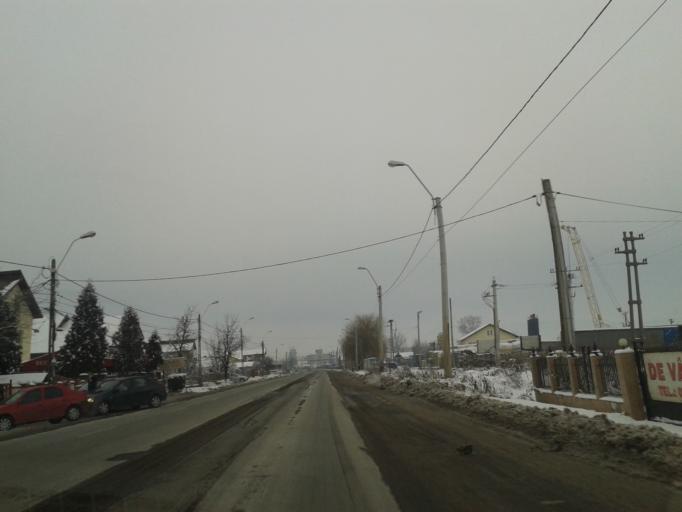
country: RO
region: Hunedoara
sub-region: Municipiul Deva
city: Cristur
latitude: 45.8298
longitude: 22.9461
